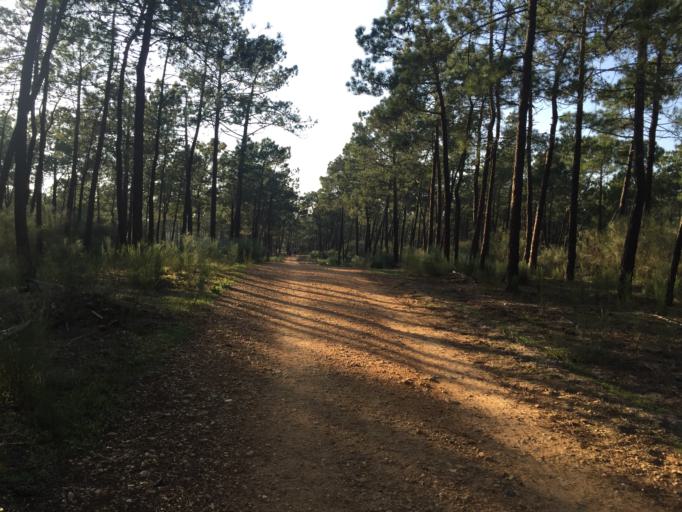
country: PT
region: Faro
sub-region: Vila Real de Santo Antonio
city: Vila Real de Santo Antonio
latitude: 37.1877
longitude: -7.4300
